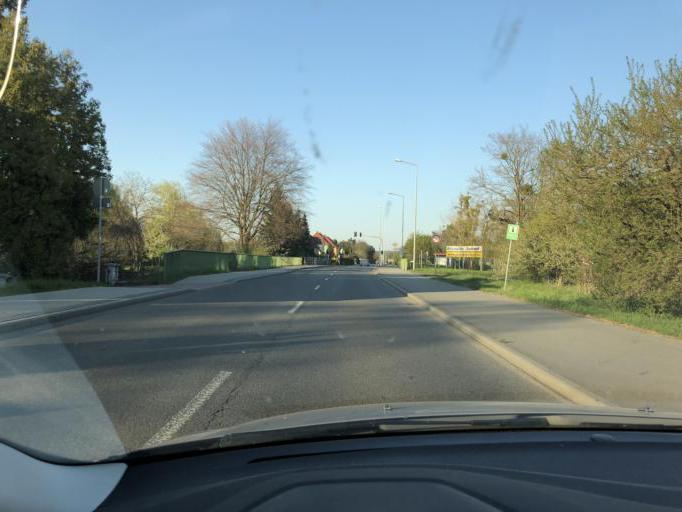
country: DE
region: Brandenburg
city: Ruhland
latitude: 51.4717
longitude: 13.8928
